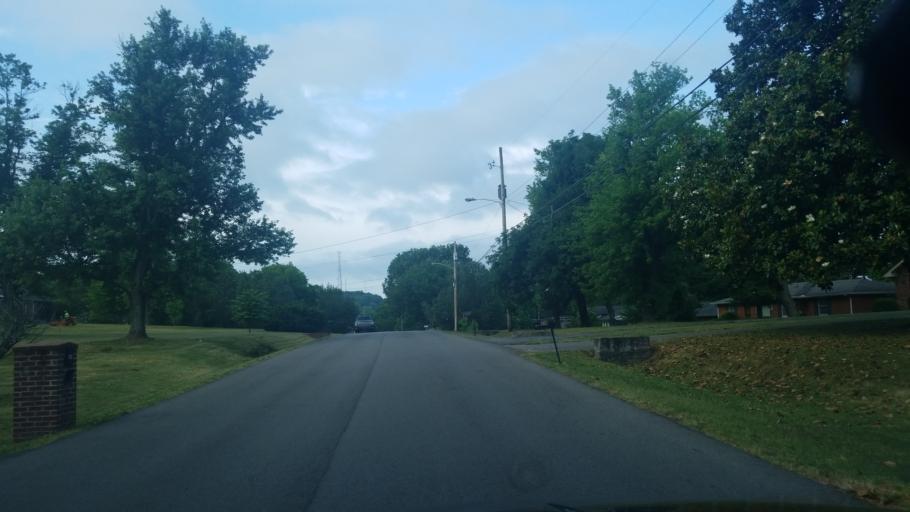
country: US
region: Tennessee
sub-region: Davidson County
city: Nashville
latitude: 36.2345
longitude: -86.7435
